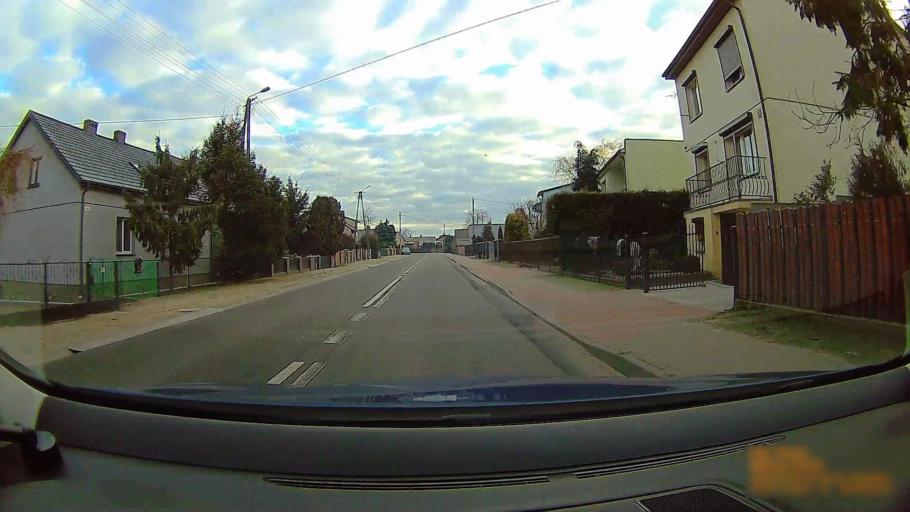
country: PL
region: Greater Poland Voivodeship
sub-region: Powiat koninski
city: Golina
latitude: 52.1937
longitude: 18.1229
